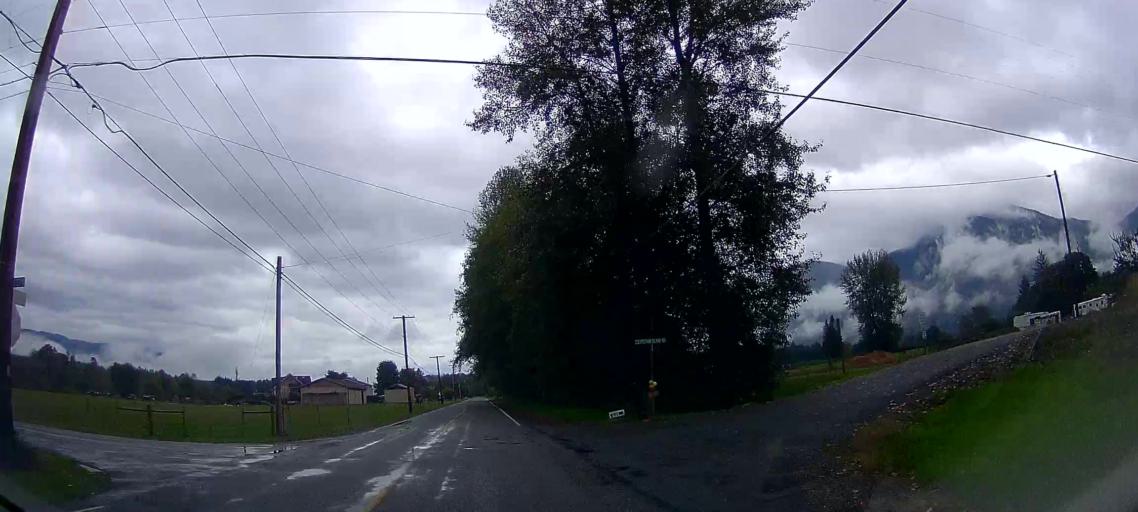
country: US
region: Washington
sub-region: Skagit County
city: Sedro-Woolley
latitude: 48.5271
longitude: -122.0388
